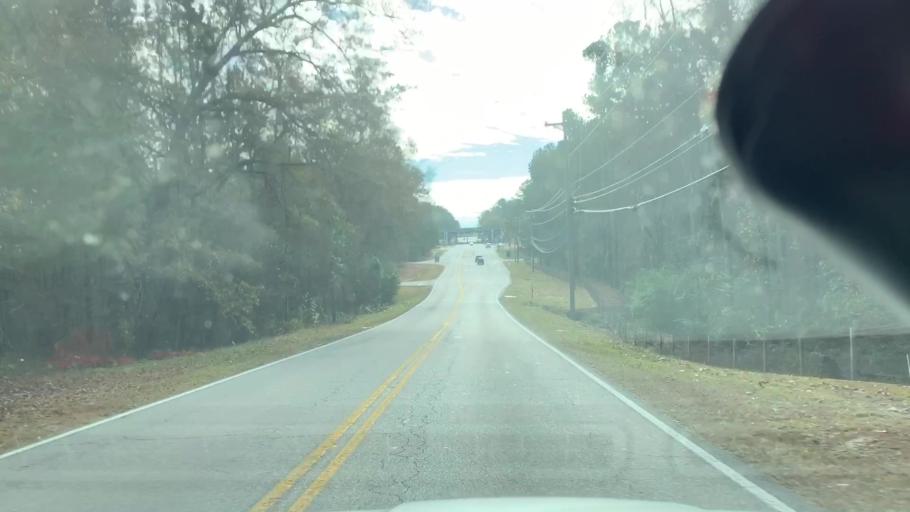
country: US
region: South Carolina
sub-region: Richland County
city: Woodfield
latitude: 34.0737
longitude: -80.9169
